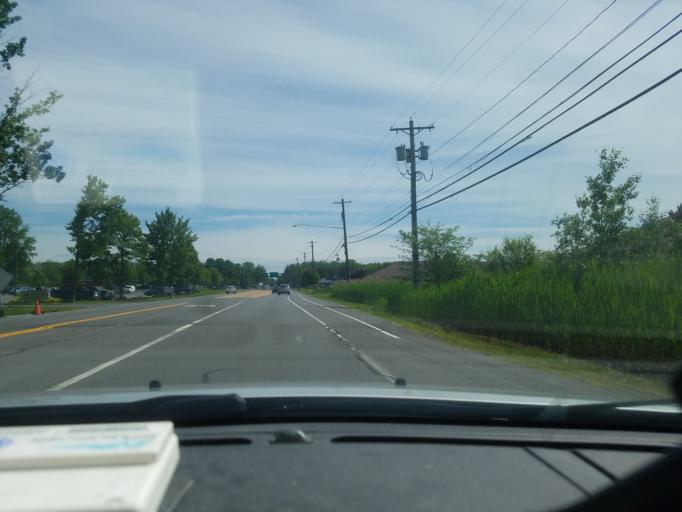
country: US
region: New York
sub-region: Onondaga County
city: East Syracuse
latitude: 43.0801
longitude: -76.0584
